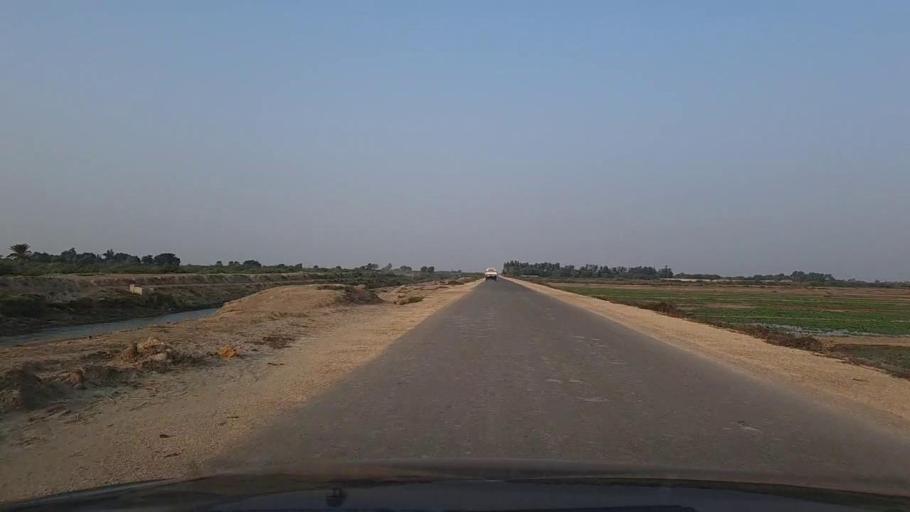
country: PK
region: Sindh
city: Mirpur Sakro
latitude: 24.4507
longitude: 67.7909
